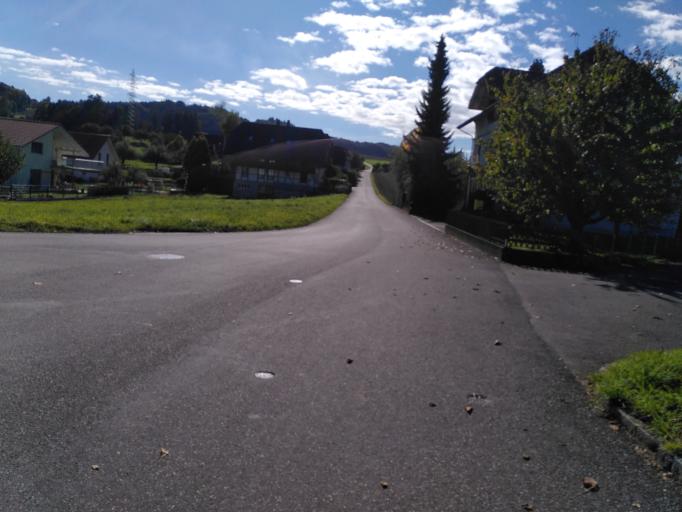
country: CH
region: Bern
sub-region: Oberaargau
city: Seeberg
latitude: 47.1407
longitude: 7.7128
